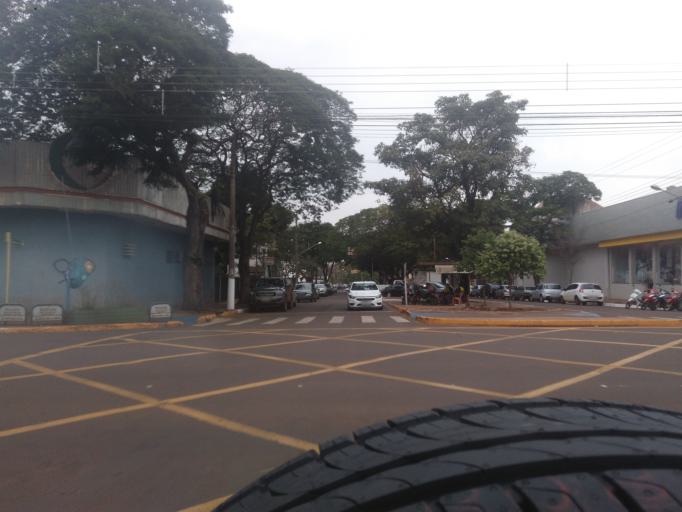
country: BR
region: Mato Grosso do Sul
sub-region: Dourados
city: Dourados
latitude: -22.2283
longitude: -54.8156
